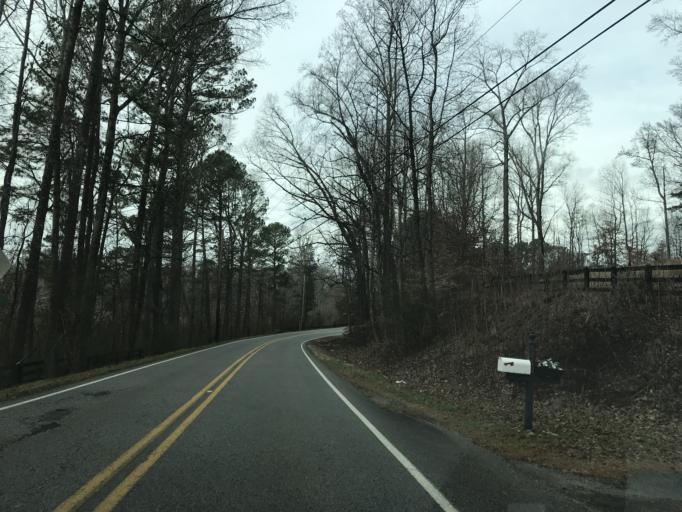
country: US
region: Georgia
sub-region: Cherokee County
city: Canton
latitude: 34.2026
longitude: -84.3901
